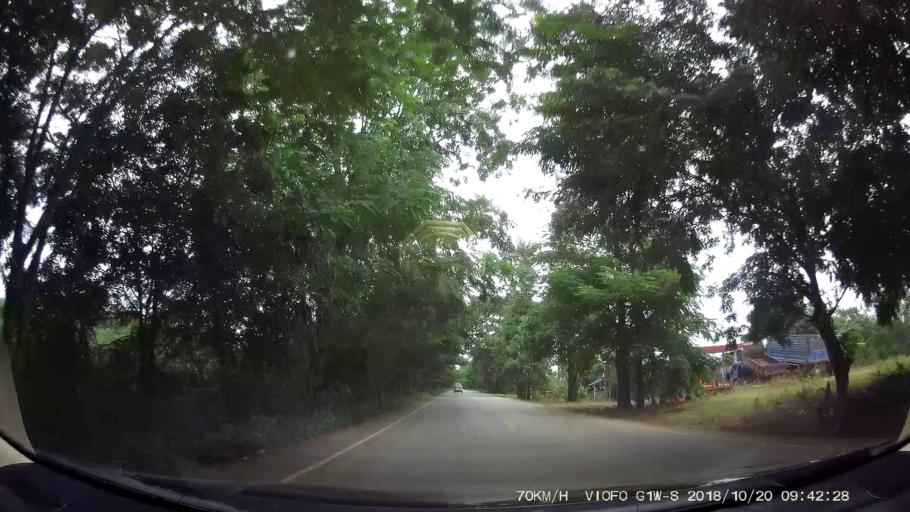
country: TH
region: Chaiyaphum
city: Khon San
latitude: 16.4640
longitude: 101.9523
